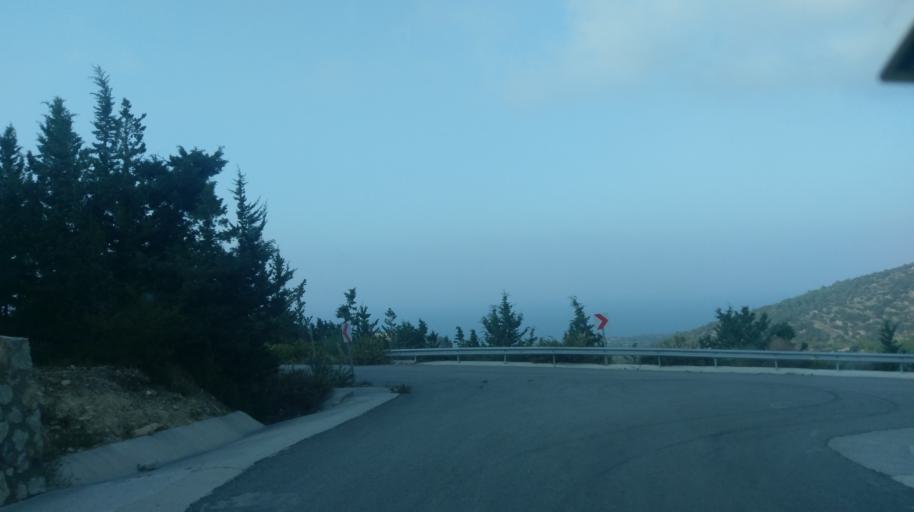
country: CY
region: Ammochostos
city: Trikomo
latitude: 35.3937
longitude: 33.8583
